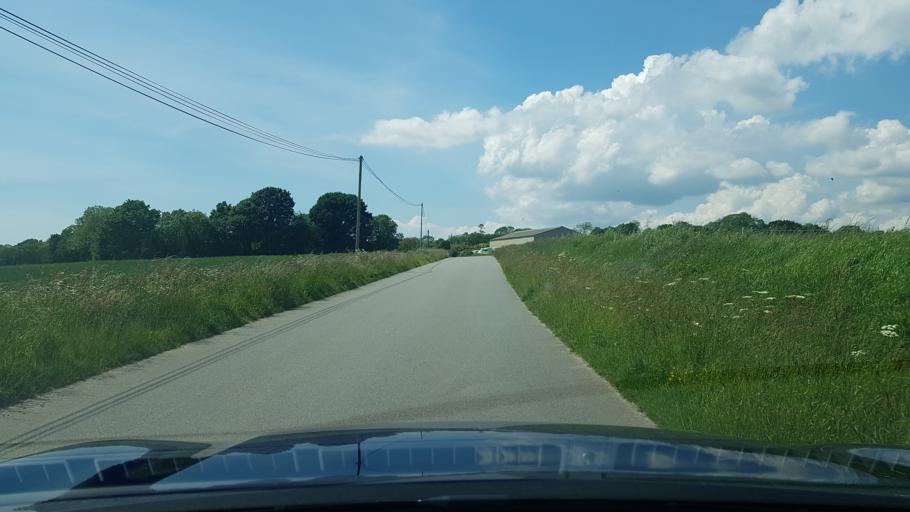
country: FR
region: Brittany
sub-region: Departement du Finistere
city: Clohars-Carnoet
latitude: 47.7920
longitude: -3.5631
